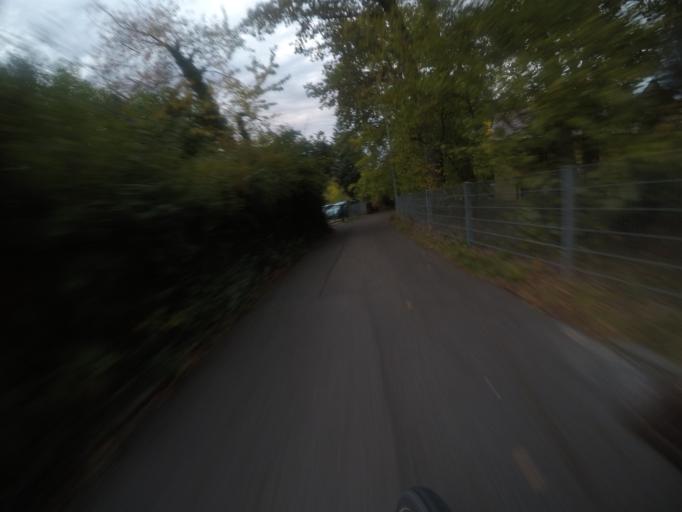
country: DE
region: Baden-Wuerttemberg
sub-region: Regierungsbezirk Stuttgart
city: Steinenbronn
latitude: 48.7213
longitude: 9.0951
